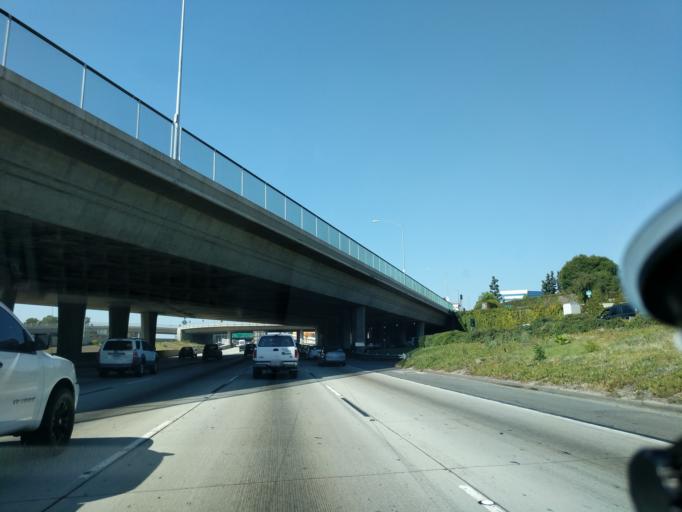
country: US
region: California
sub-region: Orange County
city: Santa Ana
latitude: 33.7677
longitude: -117.8671
